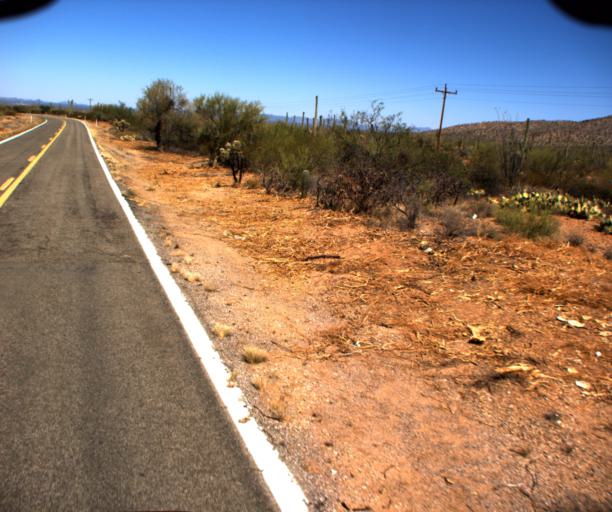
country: US
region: Arizona
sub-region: Pima County
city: Sells
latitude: 32.1762
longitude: -112.2339
